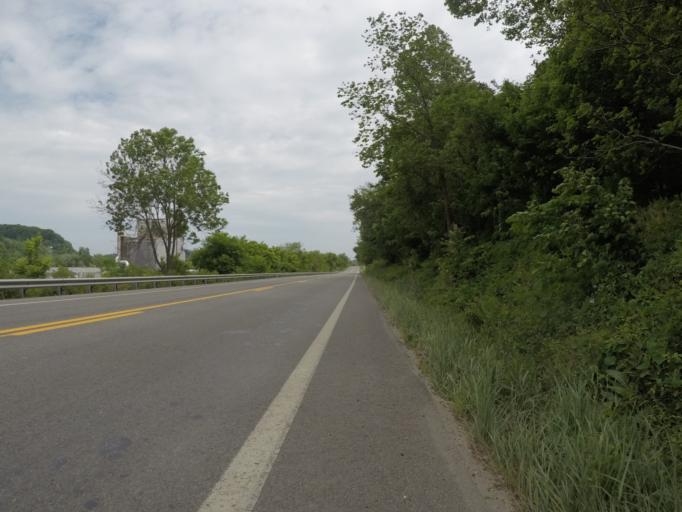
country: US
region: West Virginia
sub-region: Wayne County
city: Kenova
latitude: 38.3546
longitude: -82.5932
